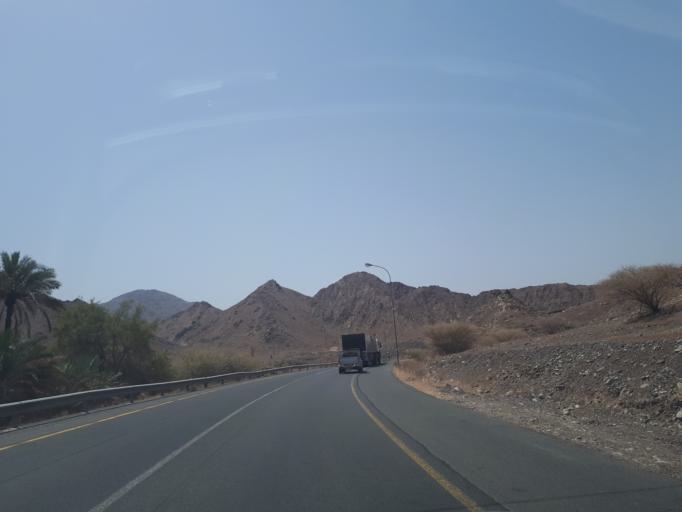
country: OM
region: Muhafazat ad Dakhiliyah
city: Sufalat Sama'il
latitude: 23.2270
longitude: 58.0797
